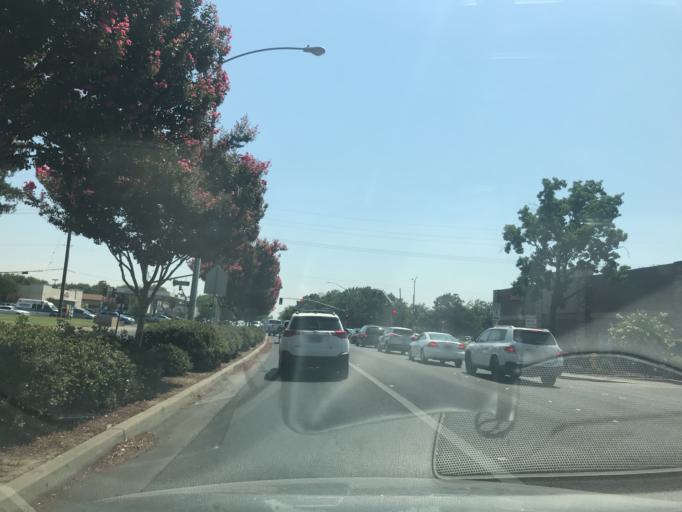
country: US
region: California
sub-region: Merced County
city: Merced
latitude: 37.3185
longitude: -120.4704
